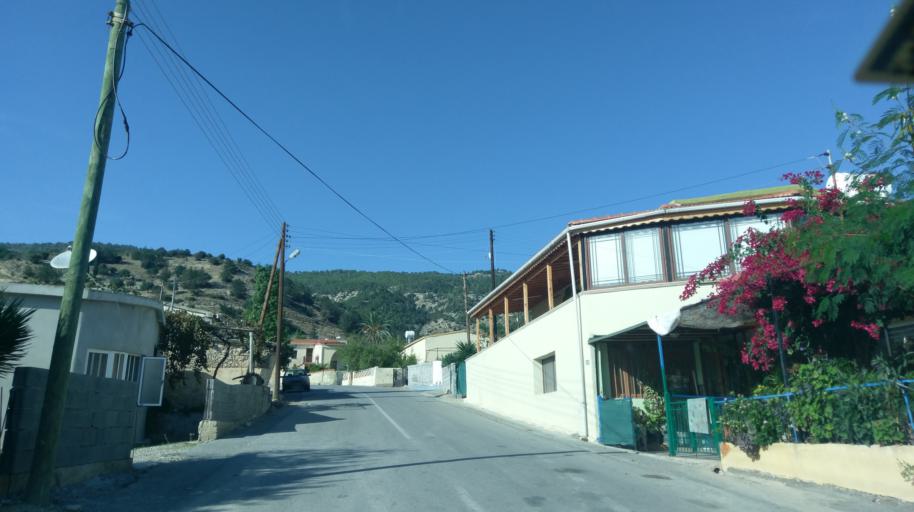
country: CY
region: Ammochostos
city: Trikomo
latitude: 35.3461
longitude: 33.7998
